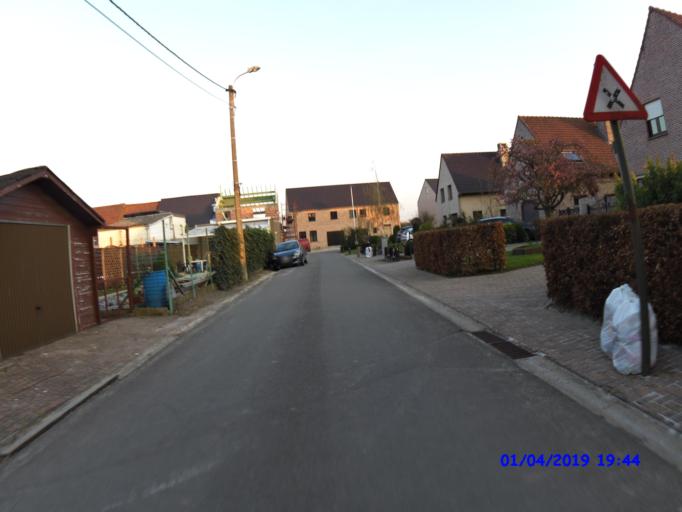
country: BE
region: Flanders
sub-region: Provincie Vlaams-Brabant
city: Opwijk
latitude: 50.9708
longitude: 4.1993
